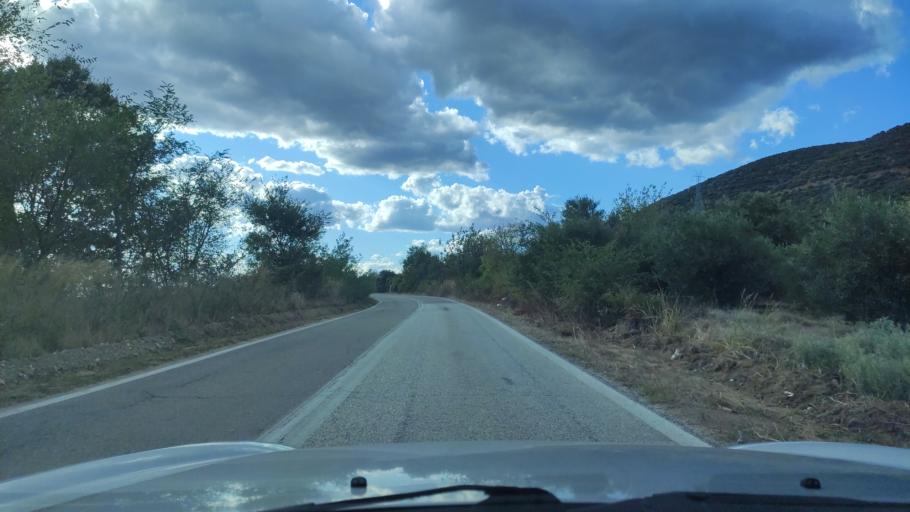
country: GR
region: East Macedonia and Thrace
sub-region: Nomos Rodopis
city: Iasmos
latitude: 41.1187
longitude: 25.1151
